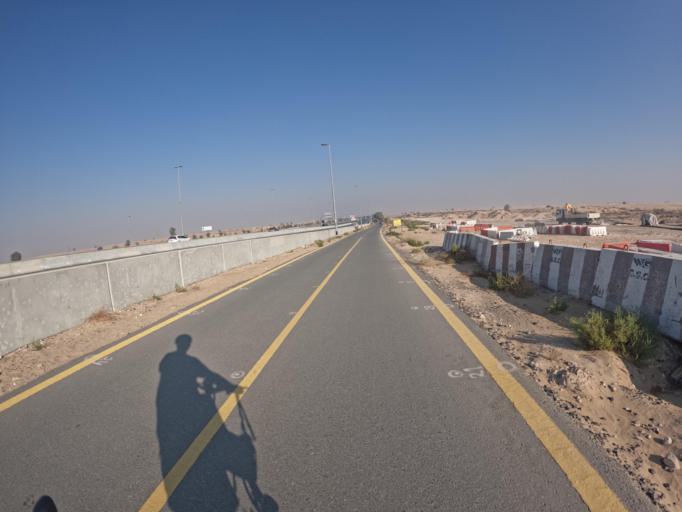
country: AE
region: Dubai
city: Dubai
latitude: 24.9535
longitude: 55.3431
